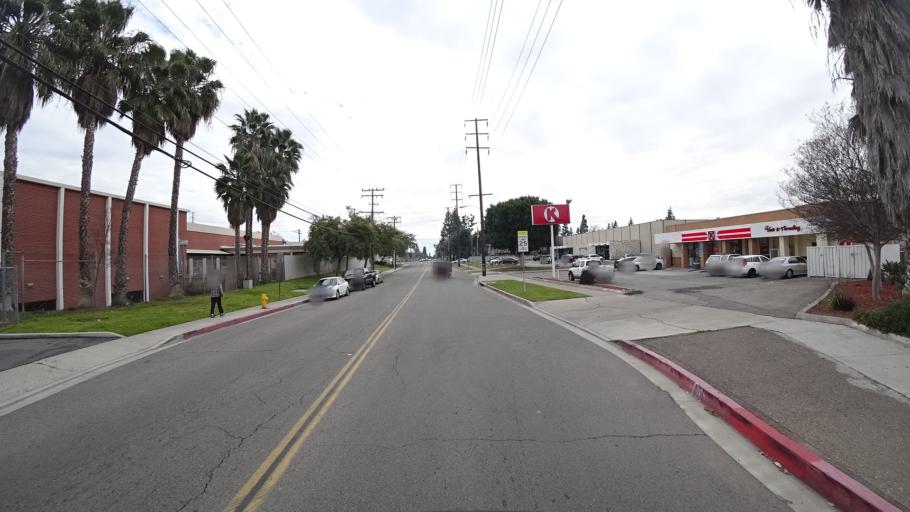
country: US
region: California
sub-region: Orange County
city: Anaheim
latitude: 33.8420
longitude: -117.9373
